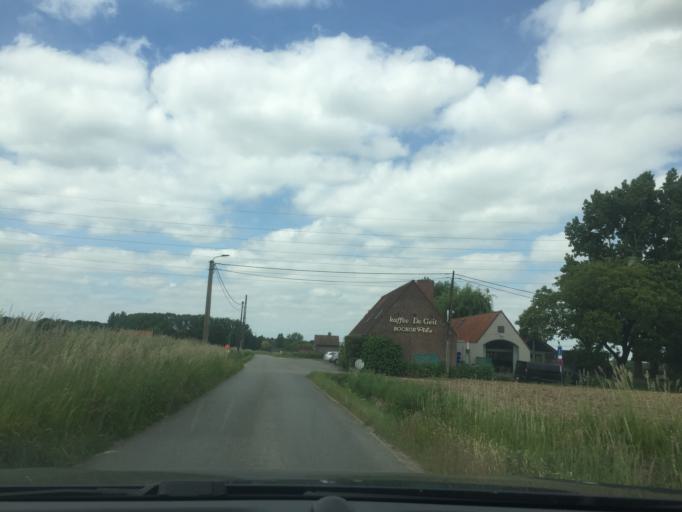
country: BE
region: Flanders
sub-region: Provincie West-Vlaanderen
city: Zwevegem
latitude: 50.7823
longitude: 3.3284
